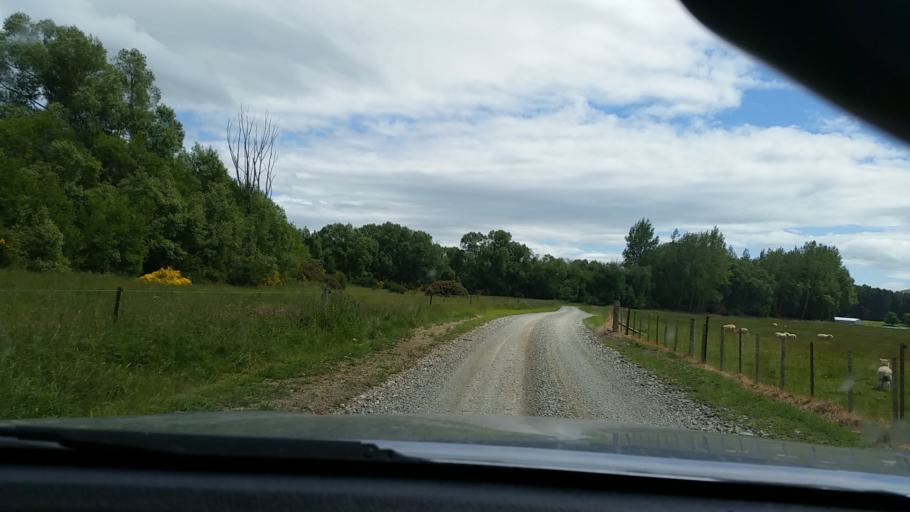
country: NZ
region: Otago
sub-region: Queenstown-Lakes District
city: Kingston
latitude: -45.7444
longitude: 168.5795
